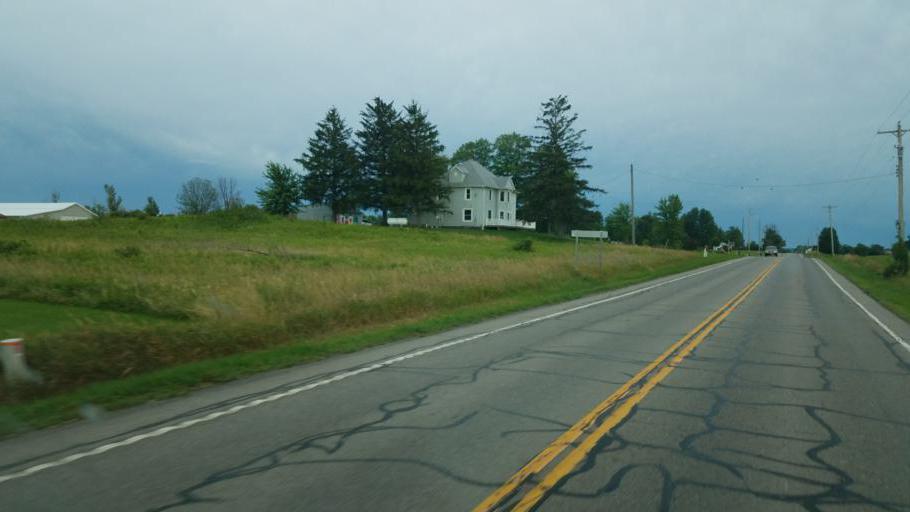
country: US
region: Ohio
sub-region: Huron County
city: Greenwich
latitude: 40.9310
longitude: -82.4963
